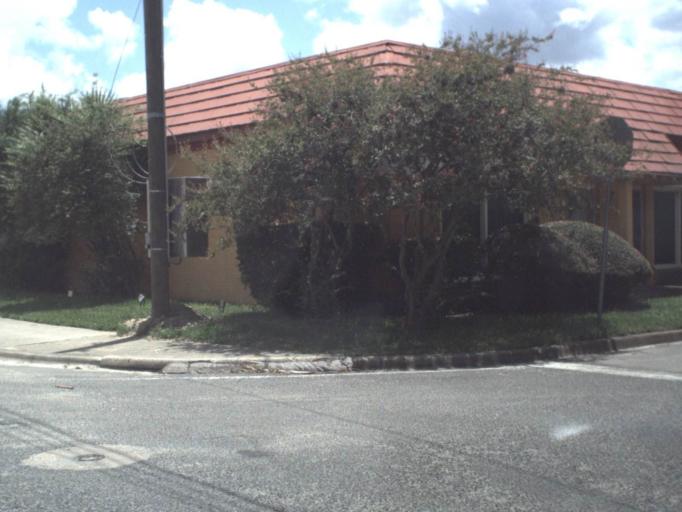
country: US
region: Florida
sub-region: Duval County
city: Jacksonville
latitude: 30.3056
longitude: -81.6455
